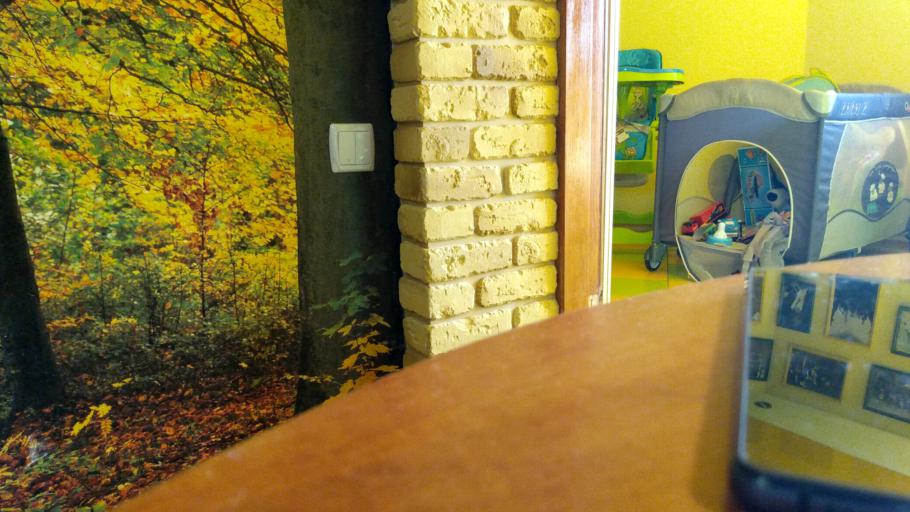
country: RU
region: Tverskaya
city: Likhoslavl'
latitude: 57.2429
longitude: 35.4412
